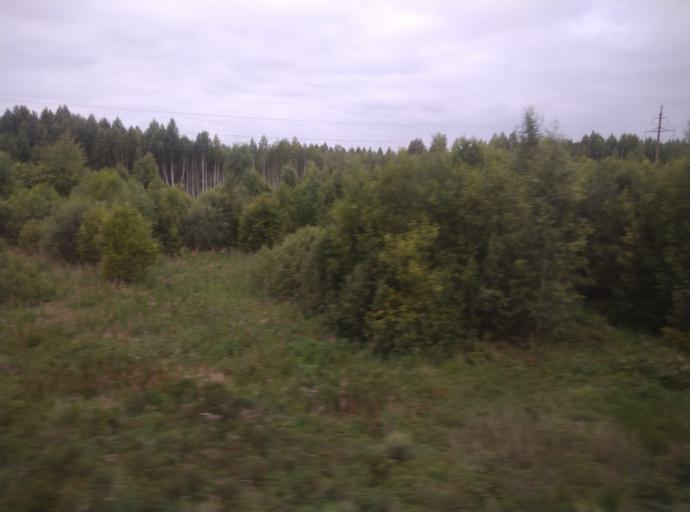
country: RU
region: Kostroma
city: Kosmynino
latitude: 57.5807
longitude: 40.7491
